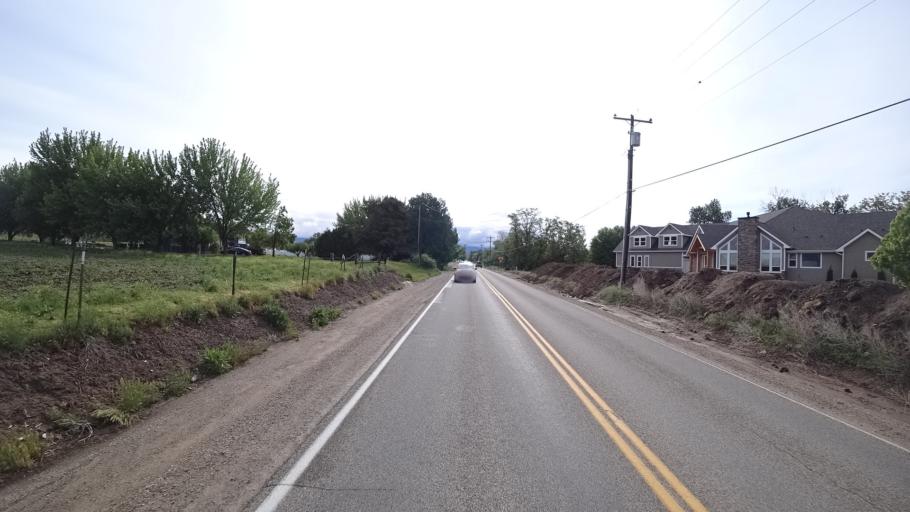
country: US
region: Idaho
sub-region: Ada County
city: Eagle
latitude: 43.7208
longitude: -116.3578
